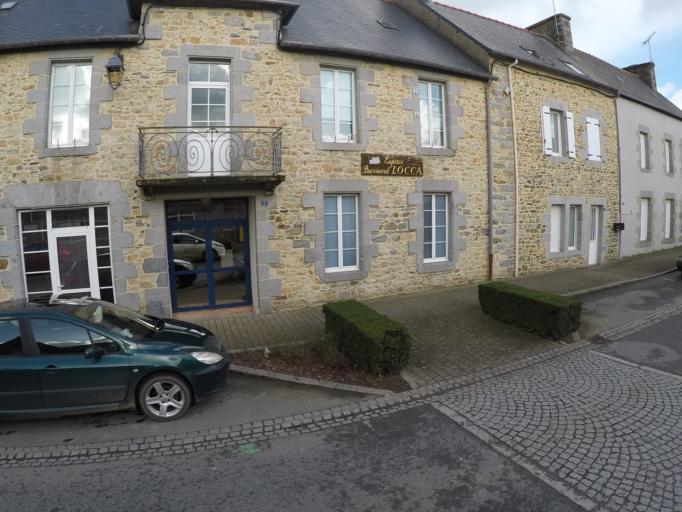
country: FR
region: Brittany
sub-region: Departement des Cotes-d'Armor
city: Lanvollon
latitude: 48.6321
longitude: -2.9870
